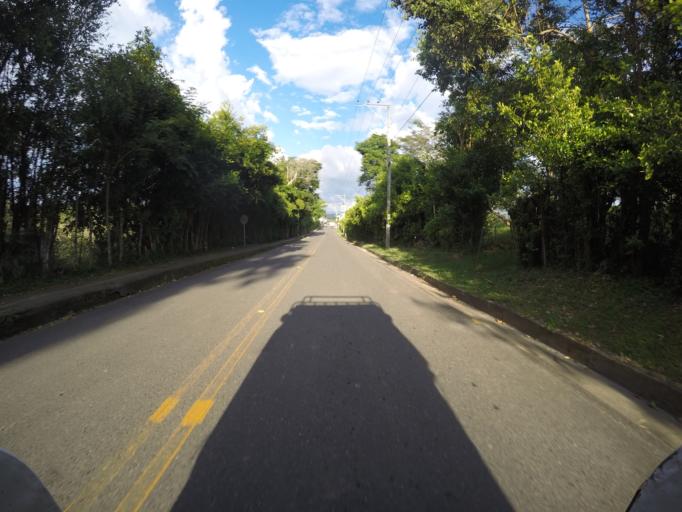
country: CO
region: Valle del Cauca
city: Alcala
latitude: 4.6764
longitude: -75.7879
